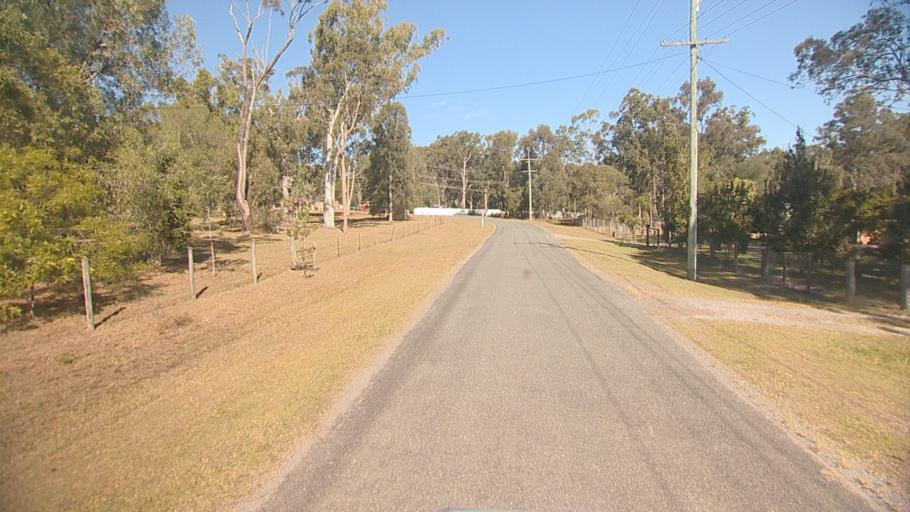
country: AU
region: Queensland
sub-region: Logan
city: Chambers Flat
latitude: -27.7776
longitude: 153.1065
